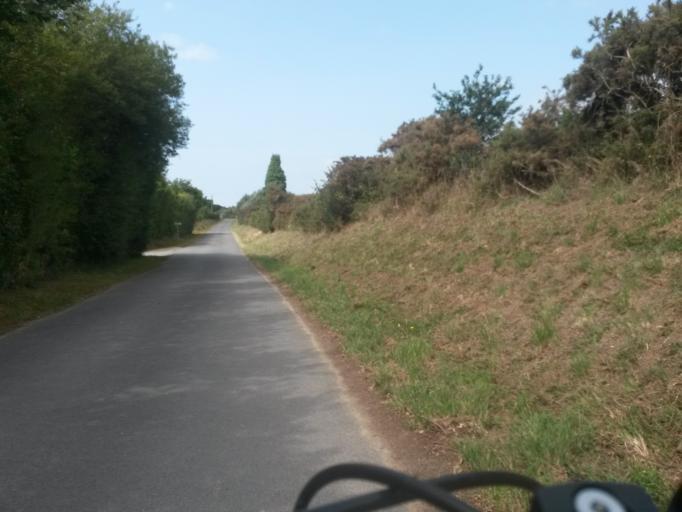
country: FR
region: Pays de la Loire
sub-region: Departement de la Loire-Atlantique
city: Guerande
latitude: 47.3121
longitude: -2.4008
